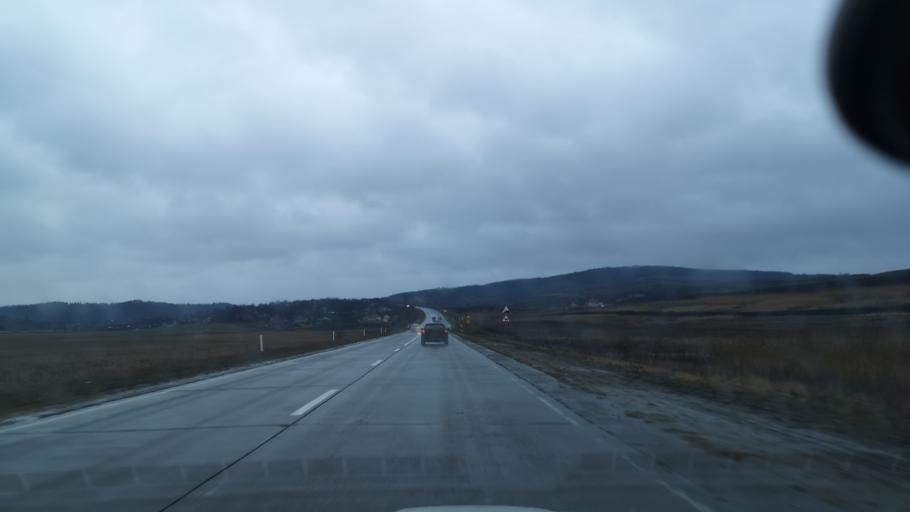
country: MD
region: Taraclia
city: Mindresti
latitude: 47.4741
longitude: 28.1778
